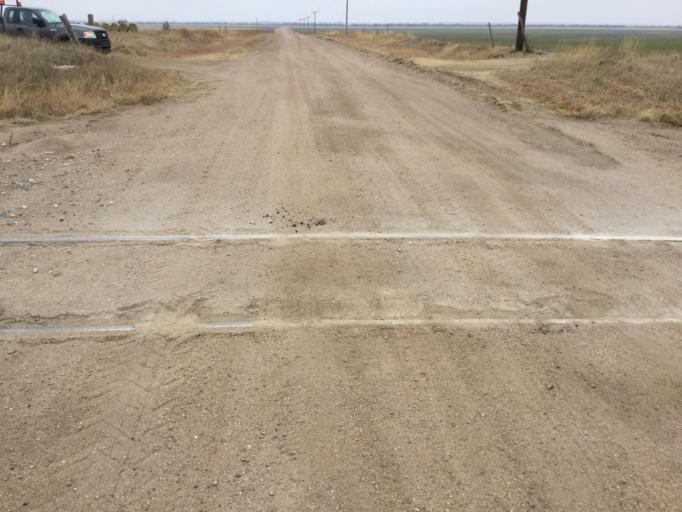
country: US
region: Kansas
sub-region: Edwards County
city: Kinsley
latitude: 38.1920
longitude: -99.5153
